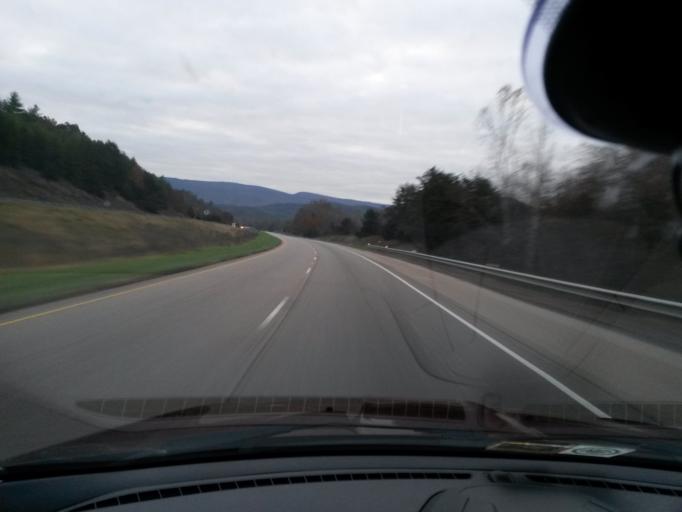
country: US
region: Virginia
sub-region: Alleghany County
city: Clifton Forge
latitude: 37.8065
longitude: -79.7394
